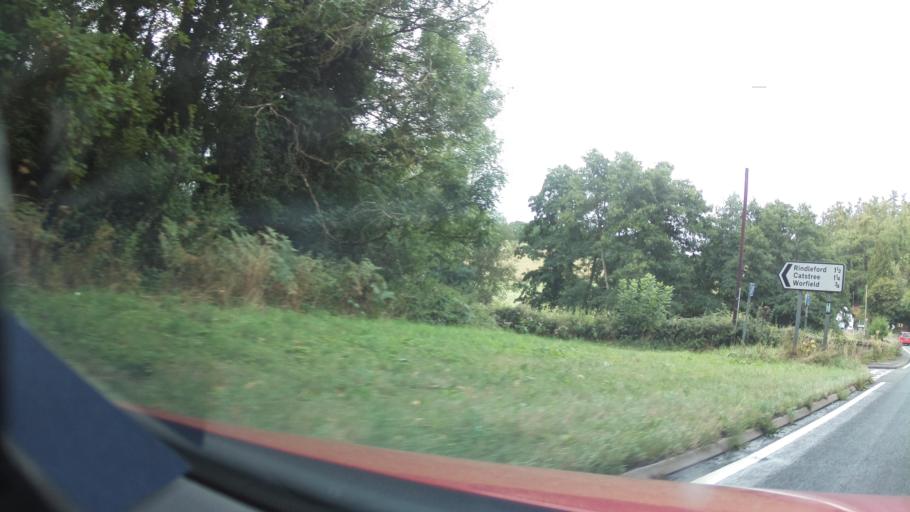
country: GB
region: England
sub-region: Shropshire
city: Bridgnorth
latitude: 52.5604
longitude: -2.3945
